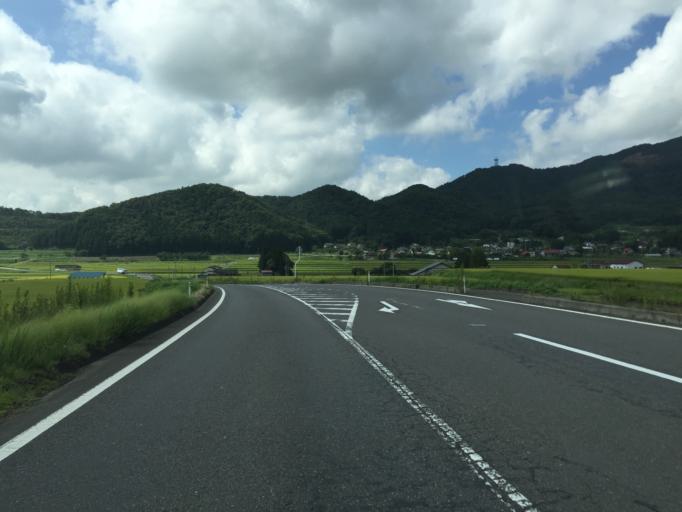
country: JP
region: Fukushima
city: Motomiya
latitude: 37.5235
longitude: 140.3738
